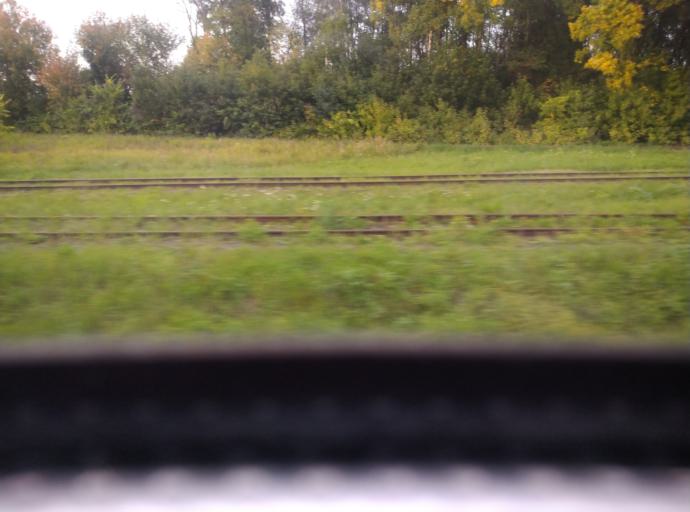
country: RU
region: Jaroslavl
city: Yaroslavl
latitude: 57.5988
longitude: 39.8515
